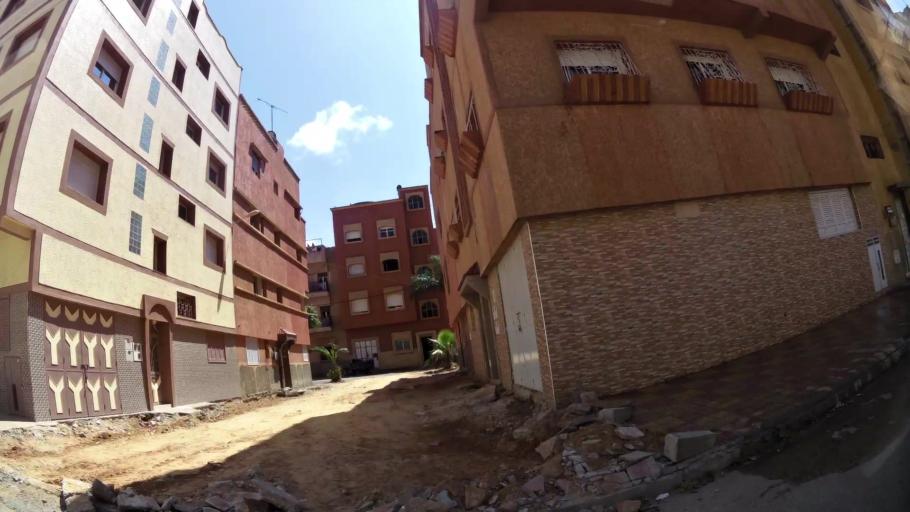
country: MA
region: Rabat-Sale-Zemmour-Zaer
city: Sale
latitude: 34.0465
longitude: -6.7915
